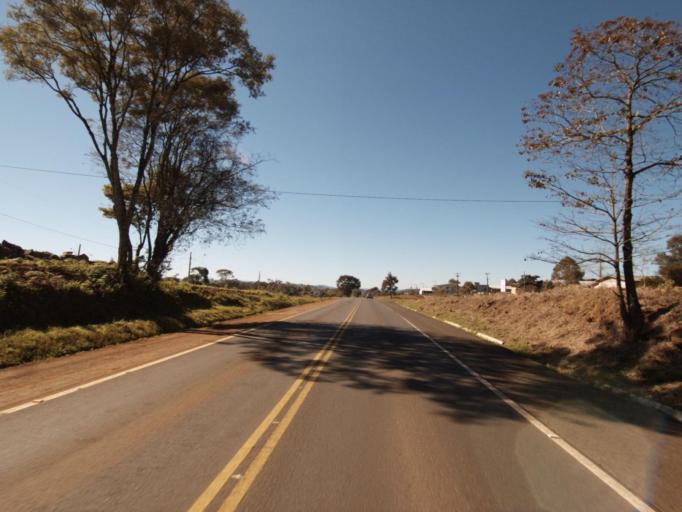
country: BR
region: Santa Catarina
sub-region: Chapeco
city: Chapeco
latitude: -26.9042
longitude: -52.8955
